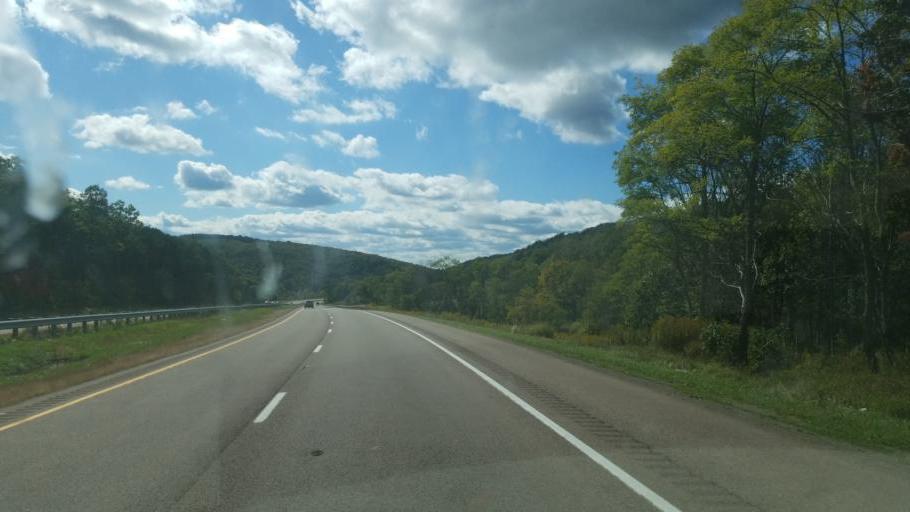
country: US
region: Pennsylvania
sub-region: Somerset County
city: Meyersdale
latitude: 39.7013
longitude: -79.3105
